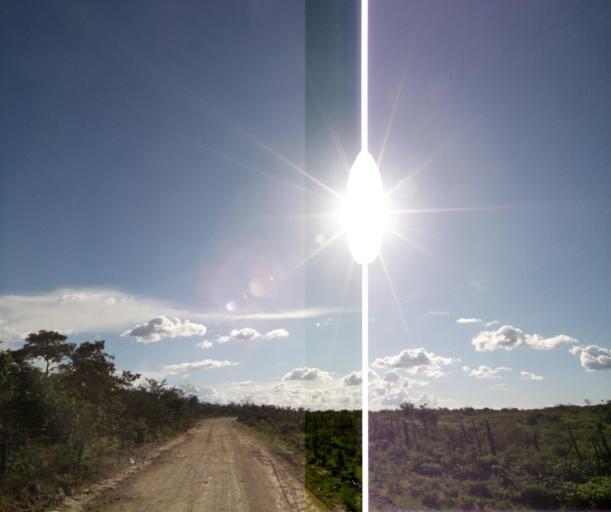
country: BR
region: Bahia
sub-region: Tanhacu
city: Tanhacu
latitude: -14.1893
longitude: -40.9667
